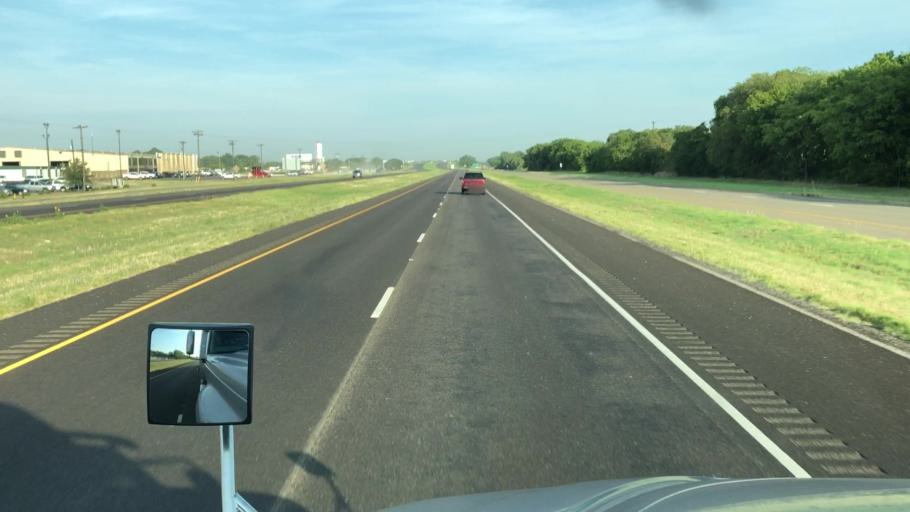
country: US
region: Texas
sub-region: McLennan County
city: Bellmead
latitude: 31.5504
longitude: -97.0798
